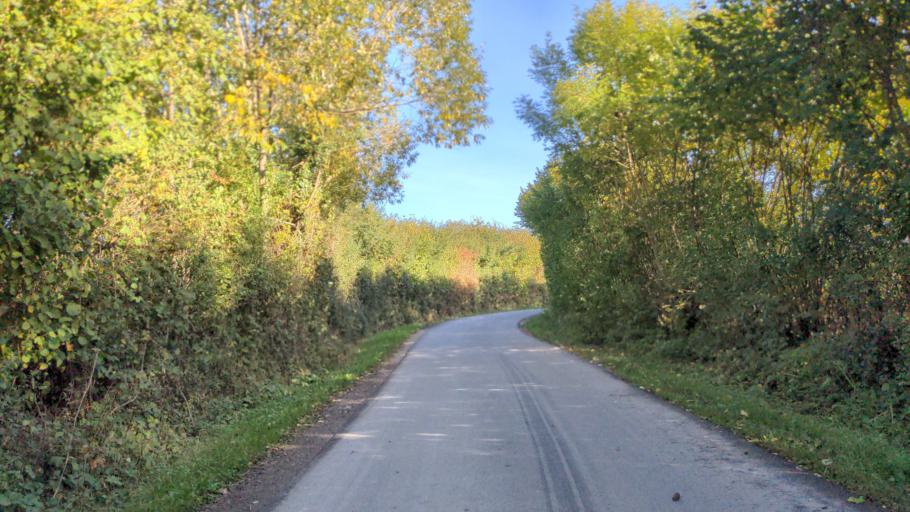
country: DE
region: Schleswig-Holstein
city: Manhagen
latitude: 54.1663
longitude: 10.9104
